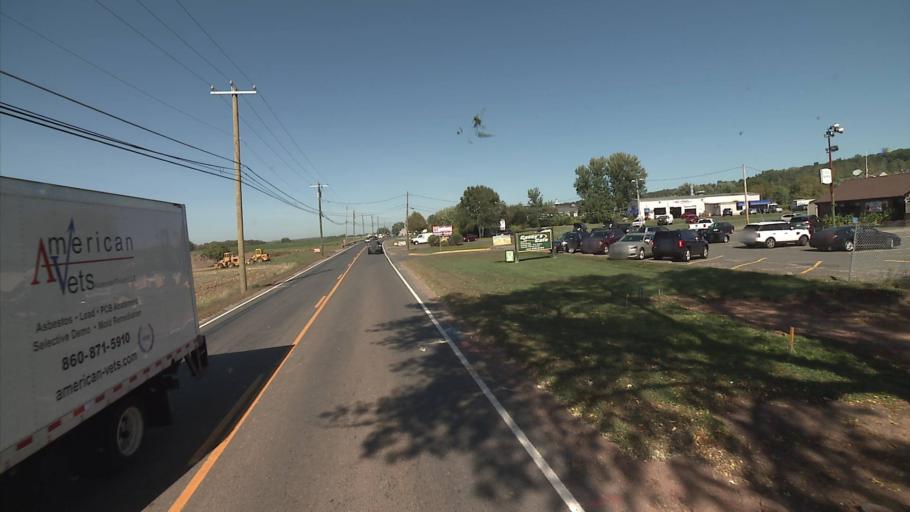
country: US
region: Connecticut
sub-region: Tolland County
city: Ellington
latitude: 41.8859
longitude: -72.4641
